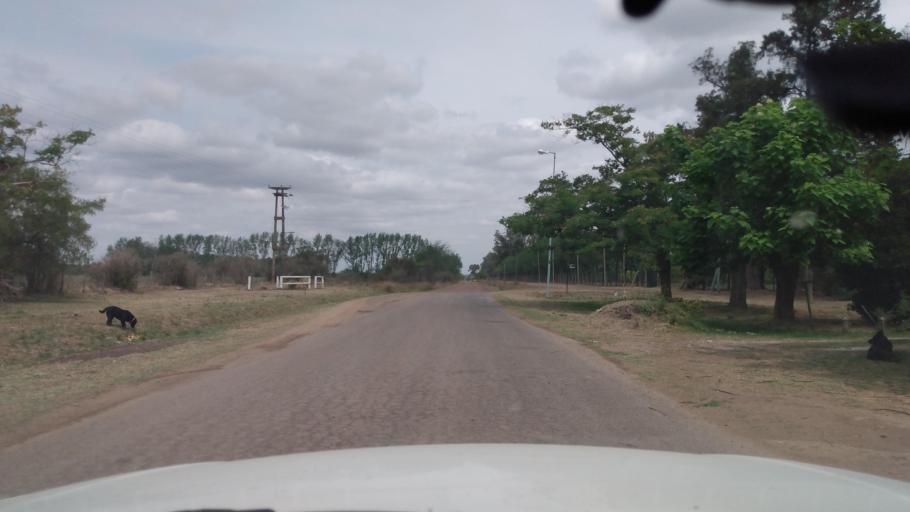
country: AR
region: Buenos Aires
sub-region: Partido de Lujan
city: Lujan
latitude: -34.5586
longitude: -59.2024
